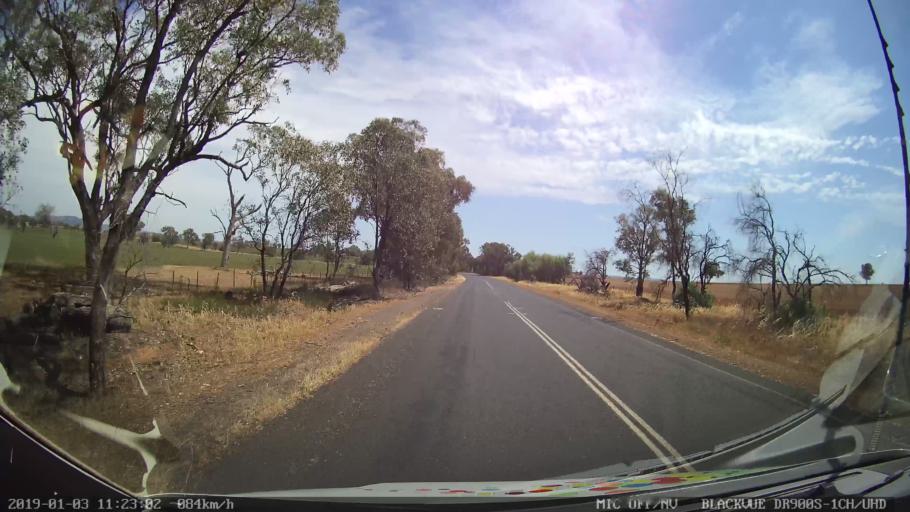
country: AU
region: New South Wales
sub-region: Weddin
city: Grenfell
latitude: -34.0680
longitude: 148.2445
